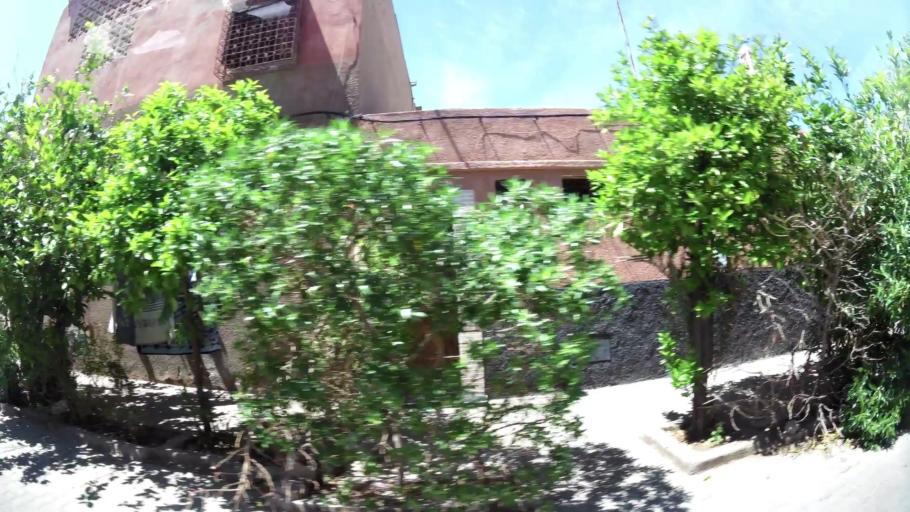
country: MA
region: Marrakech-Tensift-Al Haouz
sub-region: Marrakech
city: Marrakesh
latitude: 31.6284
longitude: -8.0433
